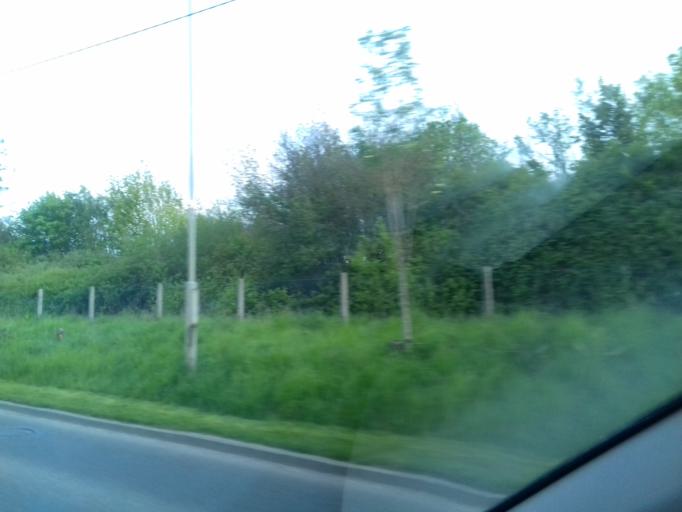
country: IE
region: Leinster
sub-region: South Dublin
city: Rathcoole
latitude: 53.2930
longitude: -6.4745
